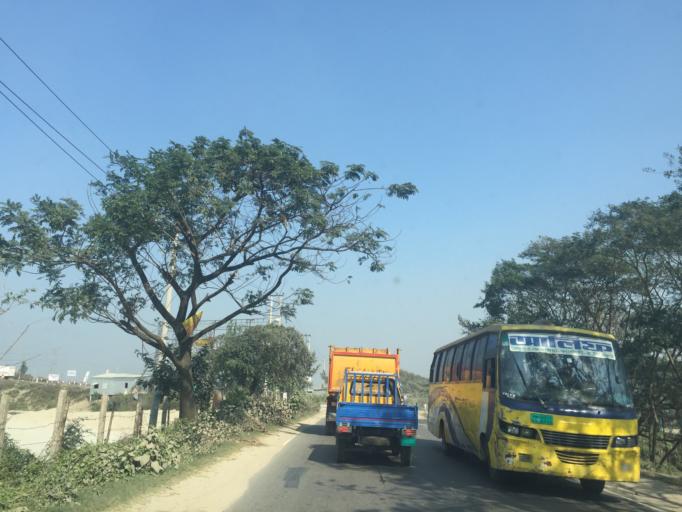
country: BD
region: Dhaka
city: Tungi
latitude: 23.8500
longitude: 90.3407
